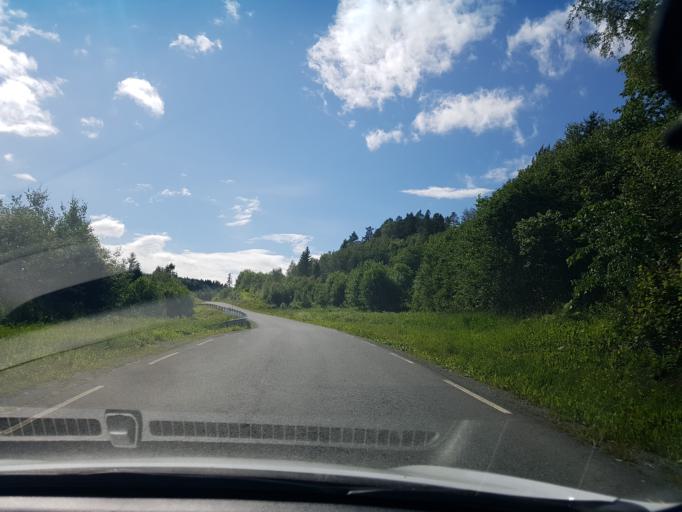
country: NO
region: Nord-Trondelag
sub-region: Frosta
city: Frosta
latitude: 63.6058
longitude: 10.8363
